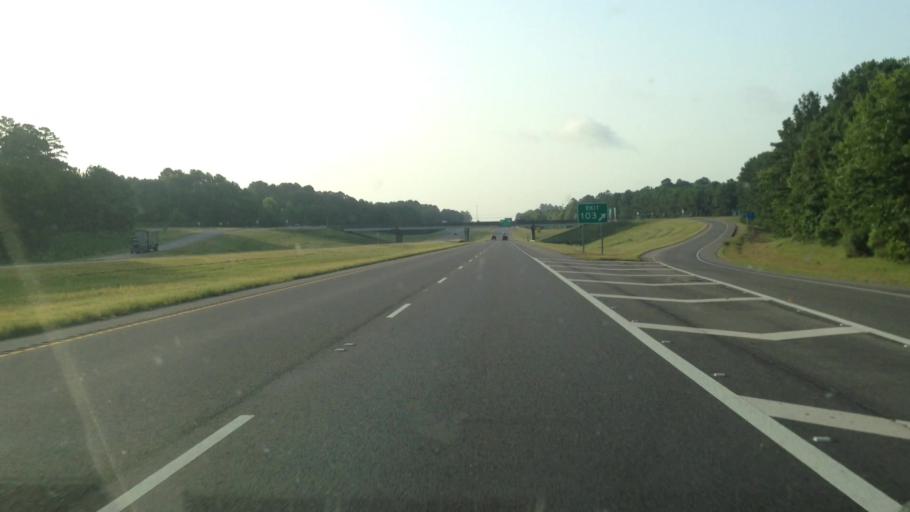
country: US
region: Louisiana
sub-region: Rapides Parish
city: Boyce
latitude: 31.4117
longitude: -92.7202
